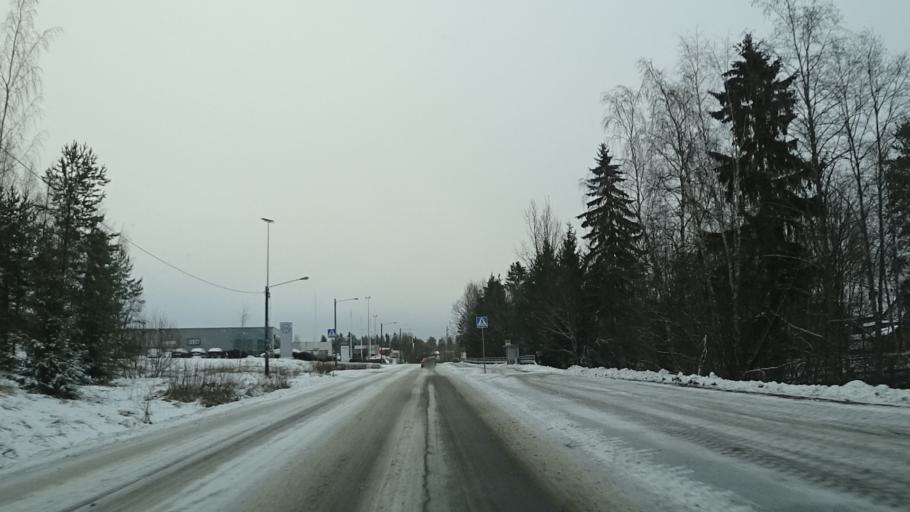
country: FI
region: Paijanne Tavastia
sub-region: Lahti
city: Lahti
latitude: 60.9454
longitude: 25.6479
